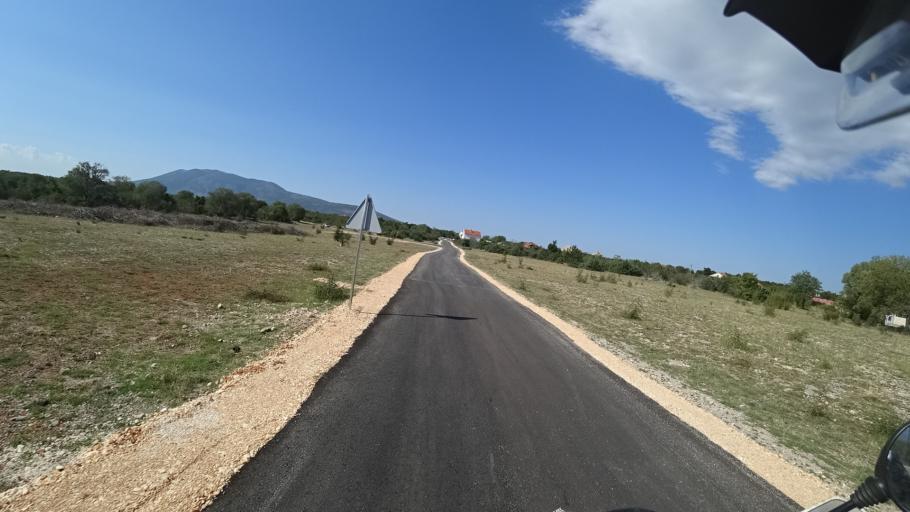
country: HR
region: Sibensko-Kniniska
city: Knin
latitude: 44.0095
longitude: 16.1926
